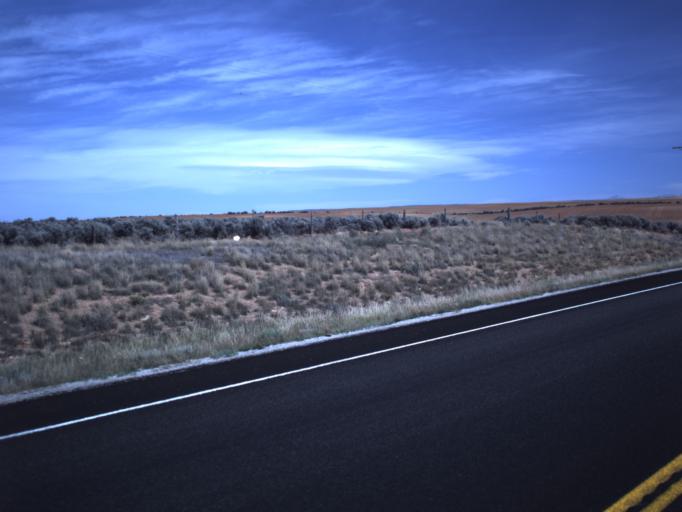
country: US
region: Utah
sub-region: San Juan County
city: Monticello
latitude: 37.8448
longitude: -109.1415
